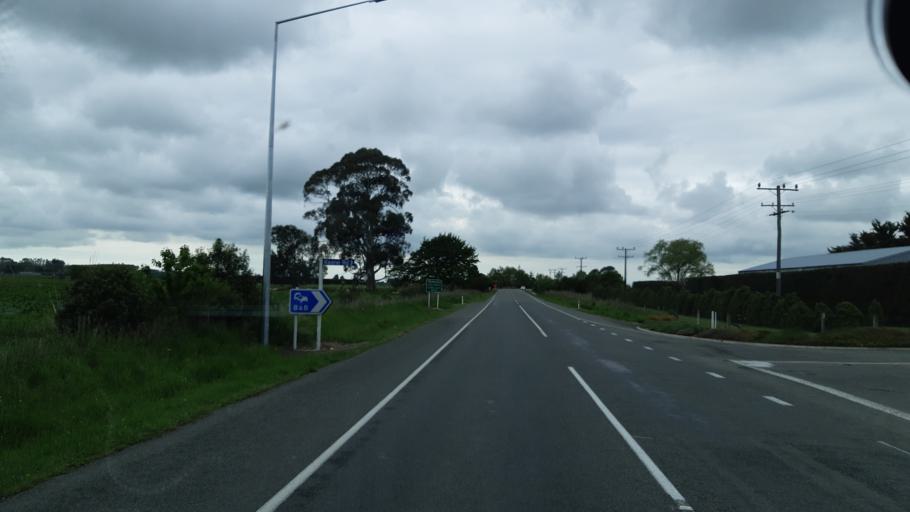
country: NZ
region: Canterbury
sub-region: Timaru District
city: Pleasant Point
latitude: -44.2678
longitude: 171.1527
